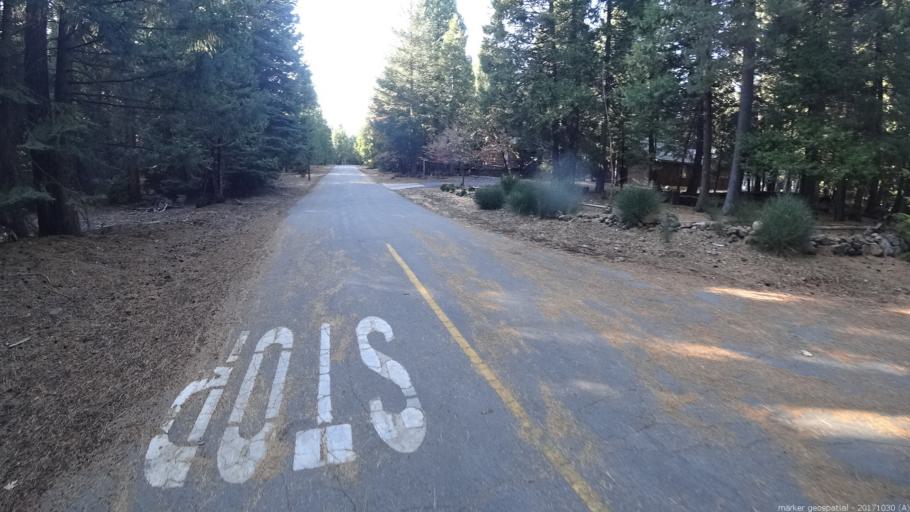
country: US
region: California
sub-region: Shasta County
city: Shingletown
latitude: 40.5547
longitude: -121.7339
